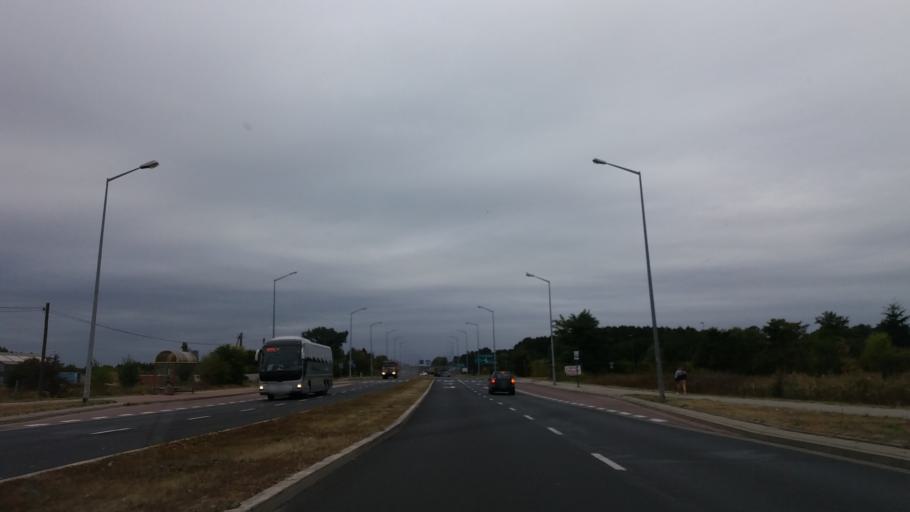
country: PL
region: Lubusz
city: Gorzow Wielkopolski
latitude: 52.7050
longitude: 15.2370
